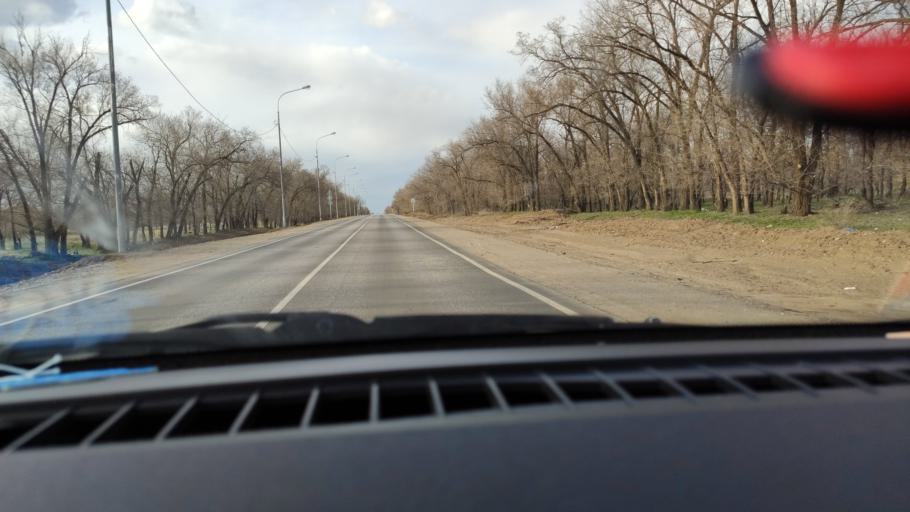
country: RU
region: Saratov
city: Krasnoarmeysk
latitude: 51.0936
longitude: 45.9560
